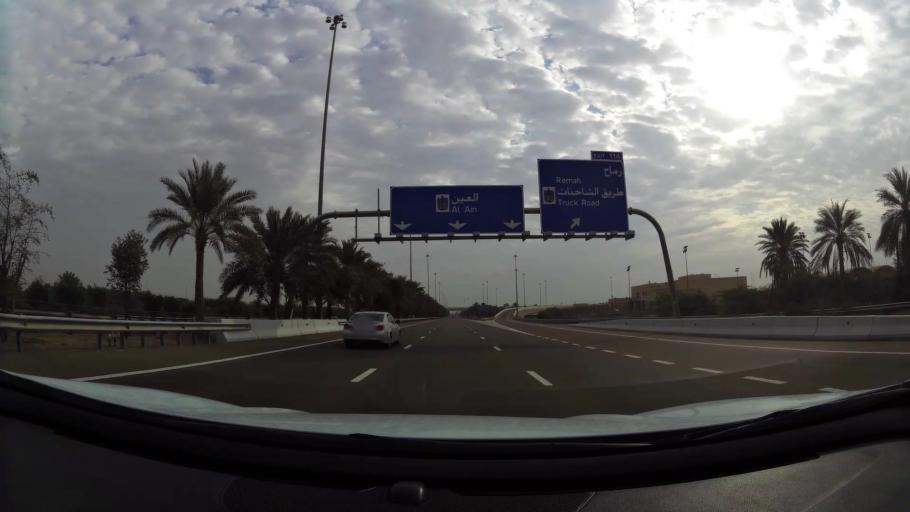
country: AE
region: Abu Dhabi
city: Al Ain
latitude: 24.1812
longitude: 55.3247
